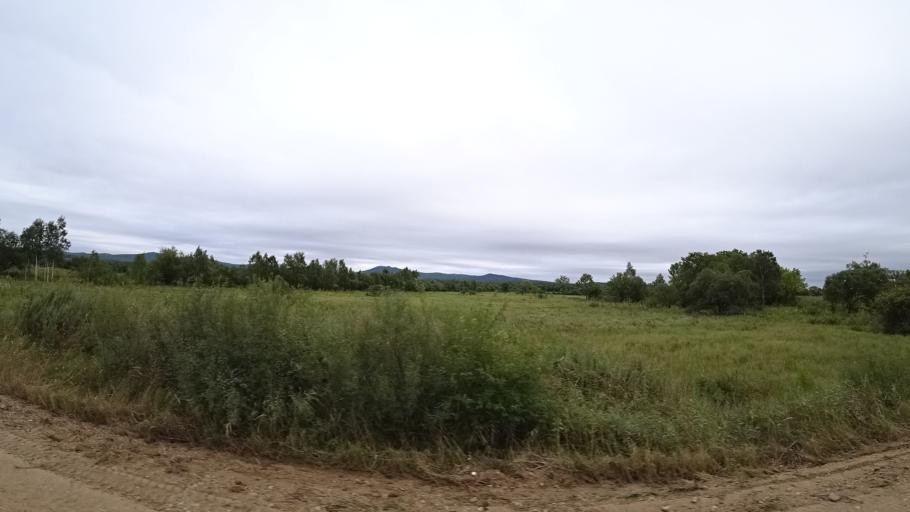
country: RU
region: Primorskiy
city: Rettikhovka
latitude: 44.1438
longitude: 132.6696
